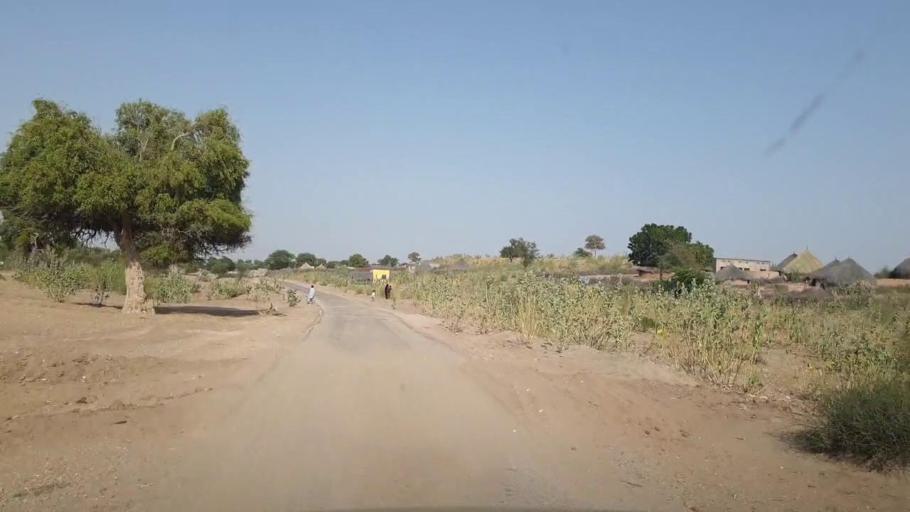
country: PK
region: Sindh
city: Islamkot
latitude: 25.1298
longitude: 70.4545
